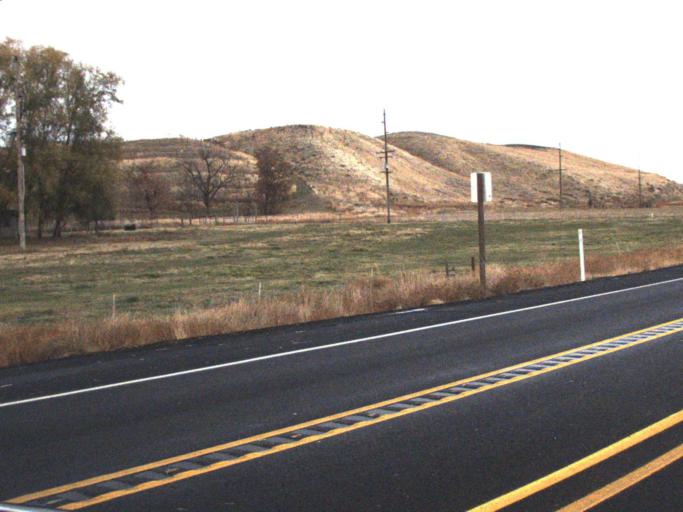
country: US
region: Washington
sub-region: Walla Walla County
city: Garrett
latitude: 46.0557
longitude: -118.5799
